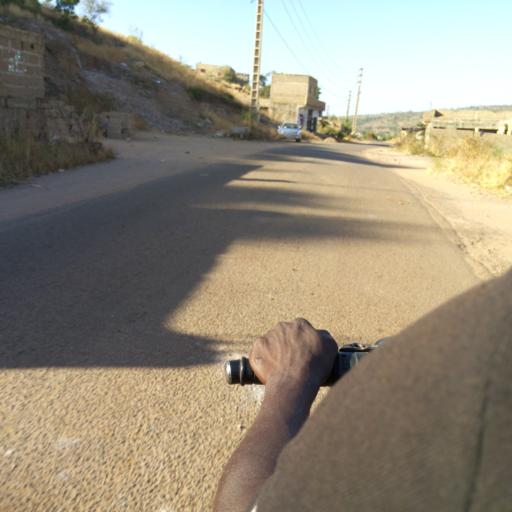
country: ML
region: Bamako
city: Bamako
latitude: 12.6593
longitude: -8.0383
